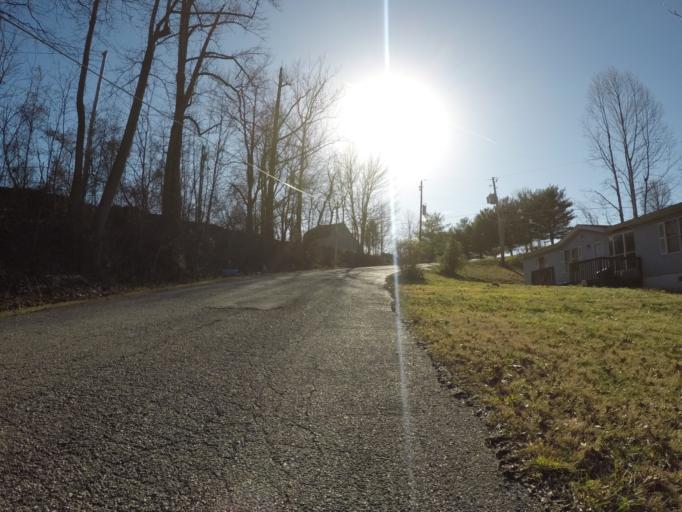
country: US
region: West Virginia
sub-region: Wayne County
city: Ceredo
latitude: 38.3880
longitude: -82.5631
